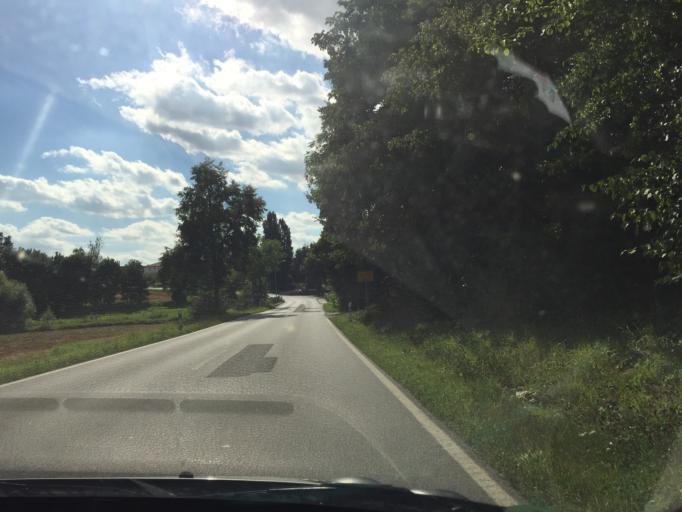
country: DE
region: Saxony
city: Bautzen
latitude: 51.1775
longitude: 14.4655
